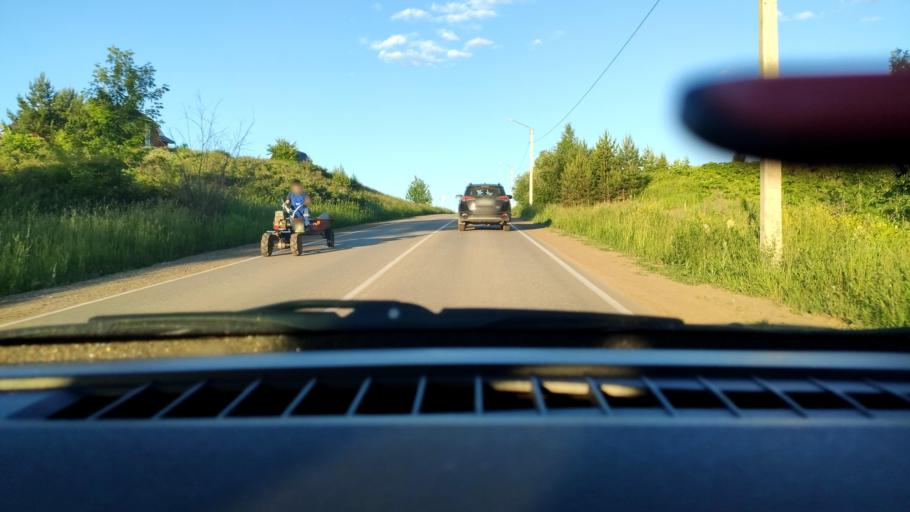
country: RU
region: Perm
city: Kultayevo
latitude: 57.9247
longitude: 55.9017
